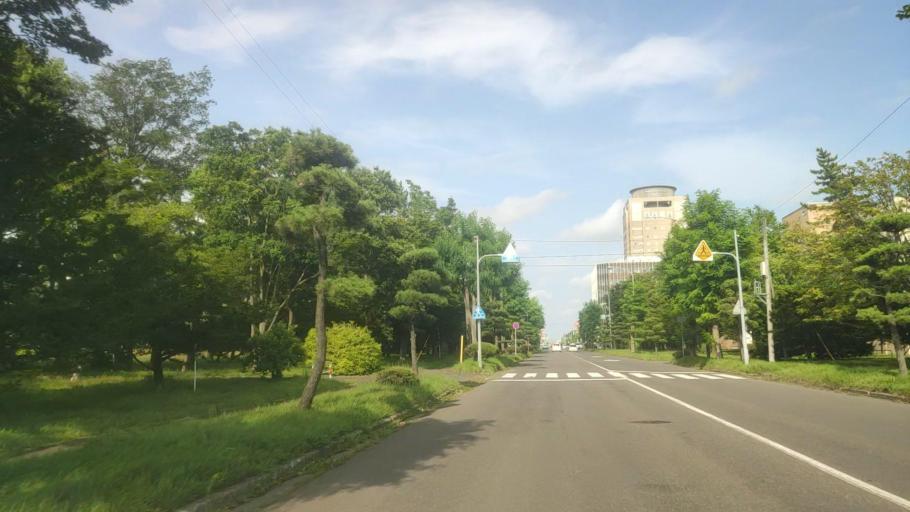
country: JP
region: Hokkaido
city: Tomakomai
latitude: 42.6364
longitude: 141.5956
